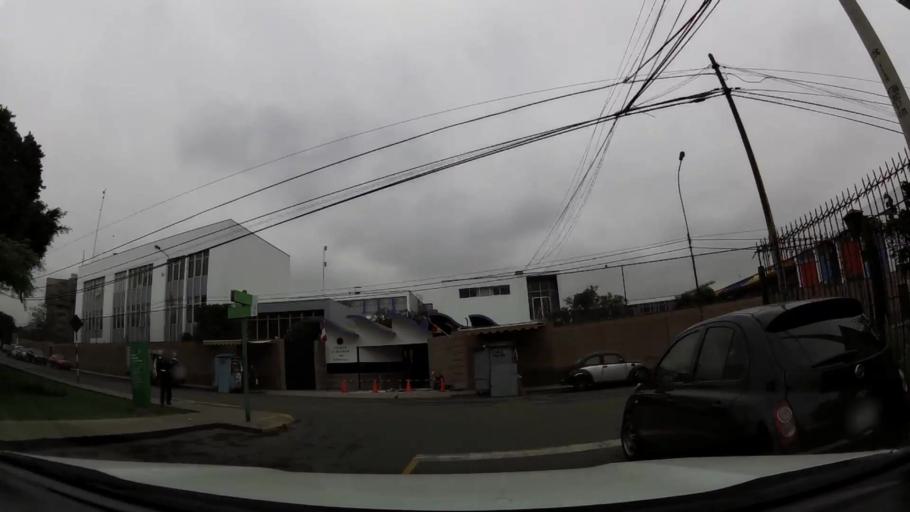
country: PE
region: Lima
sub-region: Lima
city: Surco
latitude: -12.1279
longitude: -77.0037
